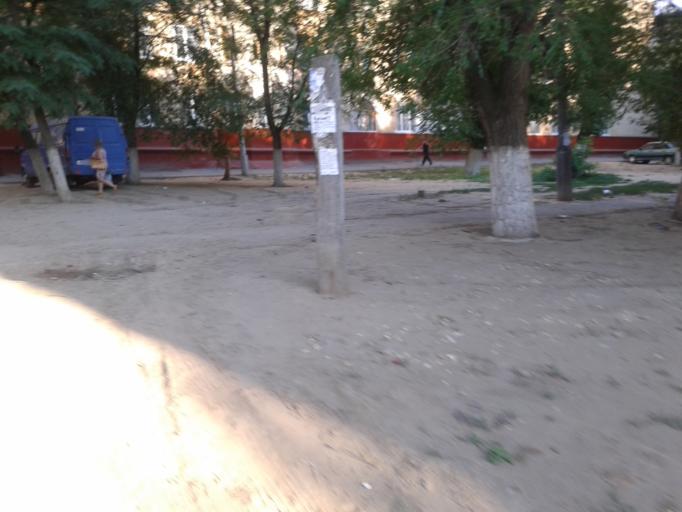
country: RU
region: Volgograd
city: Vodstroy
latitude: 48.7987
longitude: 44.6001
